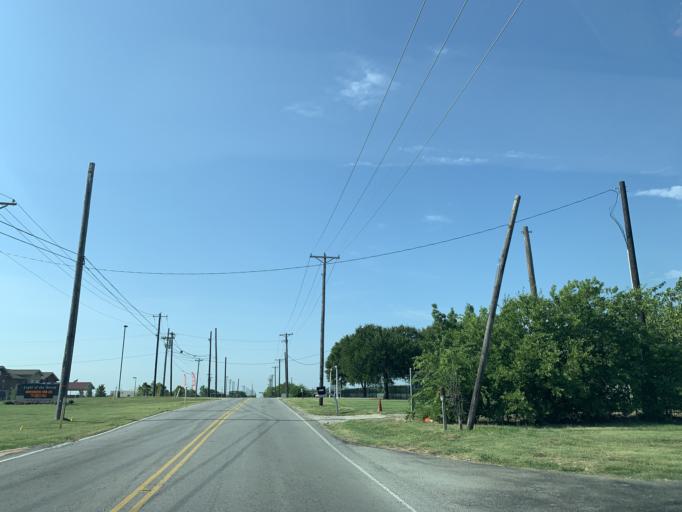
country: US
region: Texas
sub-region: Tarrant County
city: Blue Mound
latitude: 32.8991
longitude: -97.3070
